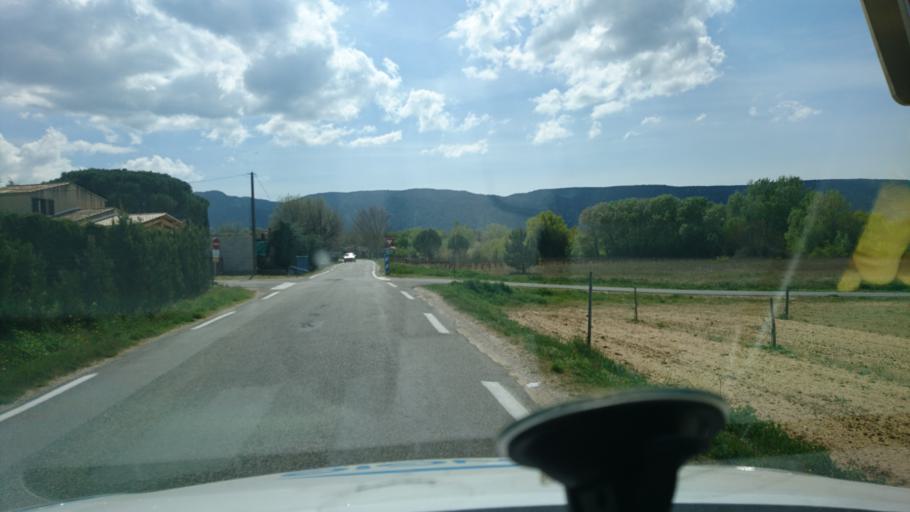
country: FR
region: Provence-Alpes-Cote d'Azur
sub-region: Departement du Vaucluse
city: Maubec
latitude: 43.8542
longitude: 5.1618
